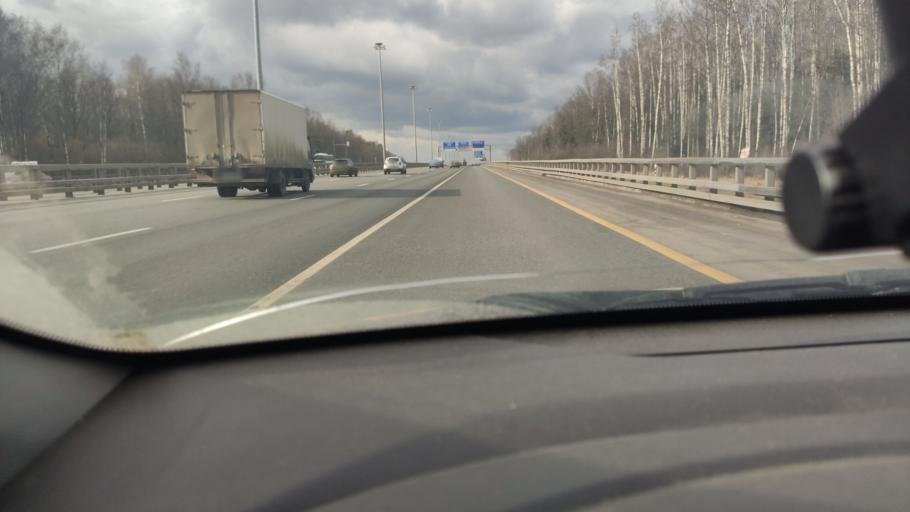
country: RU
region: Moscow
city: Vnukovo
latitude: 55.5770
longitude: 37.2248
